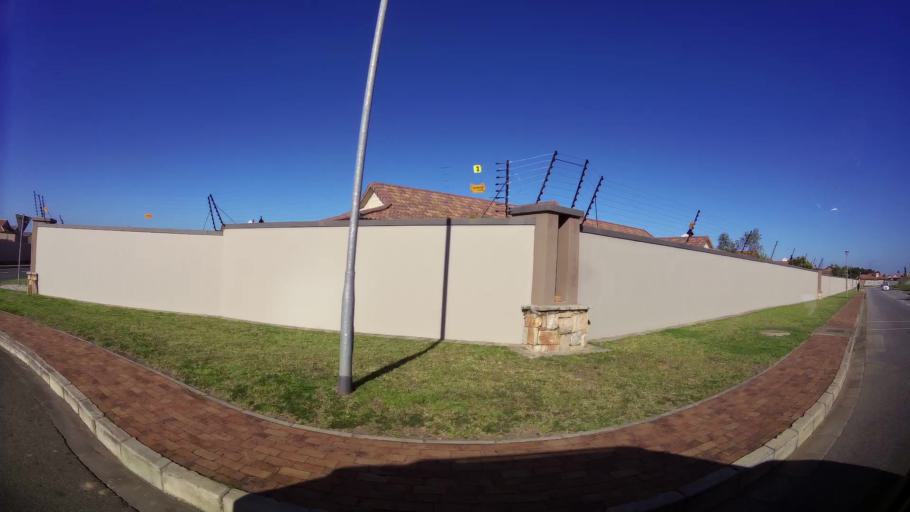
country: ZA
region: Western Cape
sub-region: Eden District Municipality
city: George
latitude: -33.9611
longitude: 22.4267
